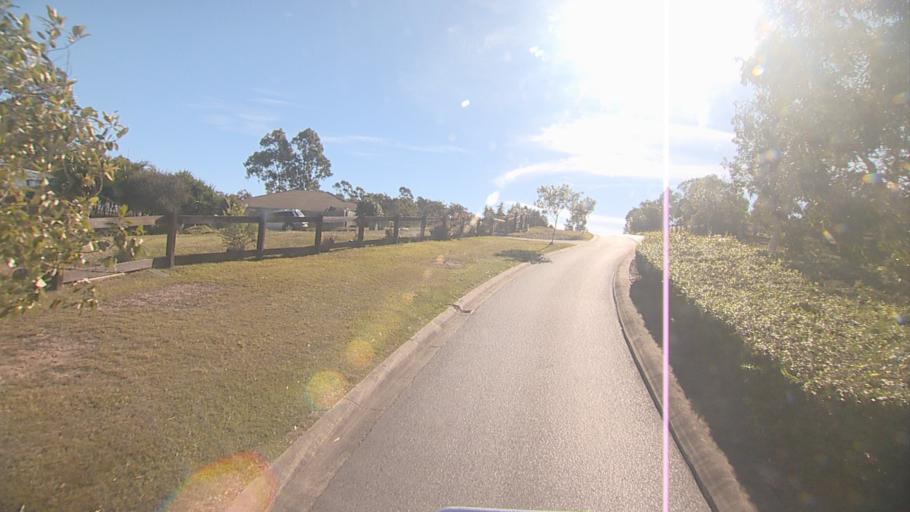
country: AU
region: Queensland
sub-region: Ipswich
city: Springfield Lakes
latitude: -27.7219
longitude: 152.9234
